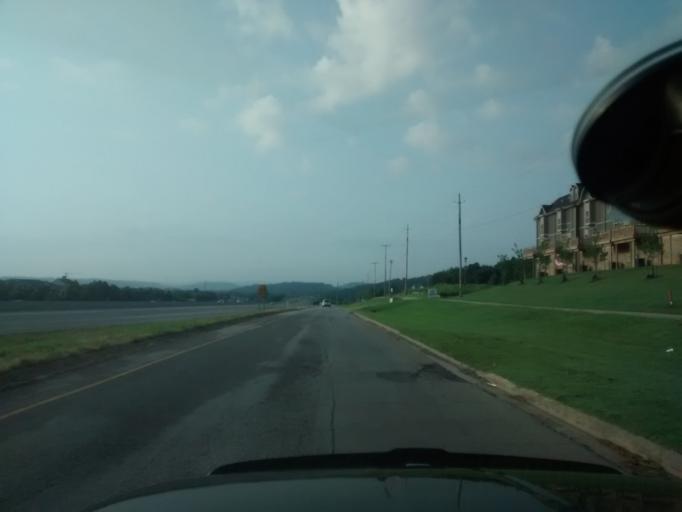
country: US
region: Arkansas
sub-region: Washington County
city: Fayetteville
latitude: 36.0620
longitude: -94.1994
